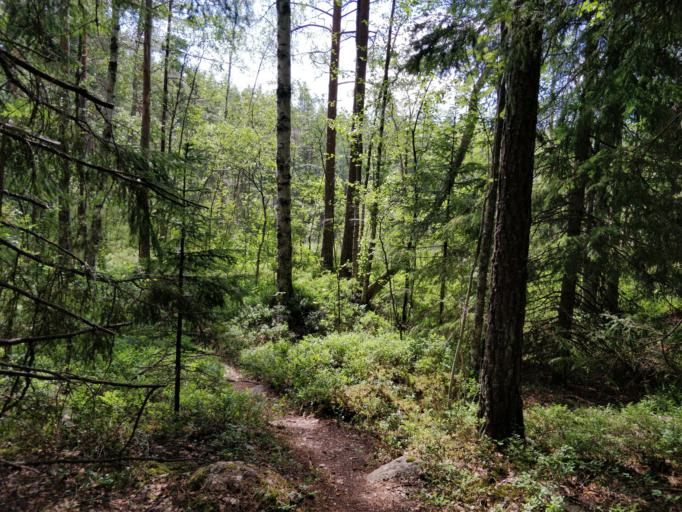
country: FI
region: Uusimaa
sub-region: Helsinki
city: Vihti
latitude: 60.3132
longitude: 24.4699
